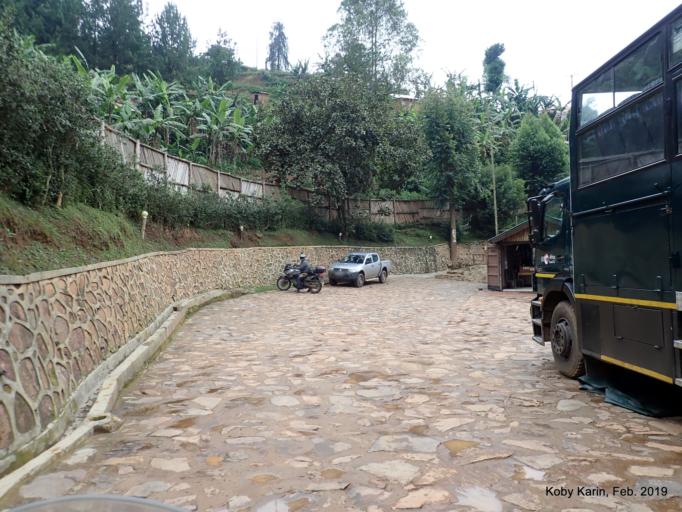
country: UG
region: Western Region
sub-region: Kabale District
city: Kabale
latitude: -1.2708
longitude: 29.9393
